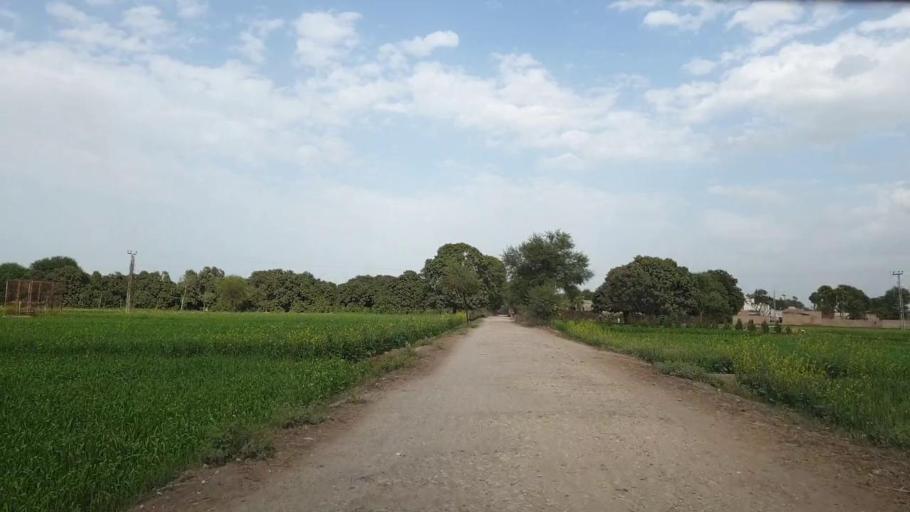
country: PK
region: Sindh
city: Matiari
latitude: 25.5621
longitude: 68.5673
